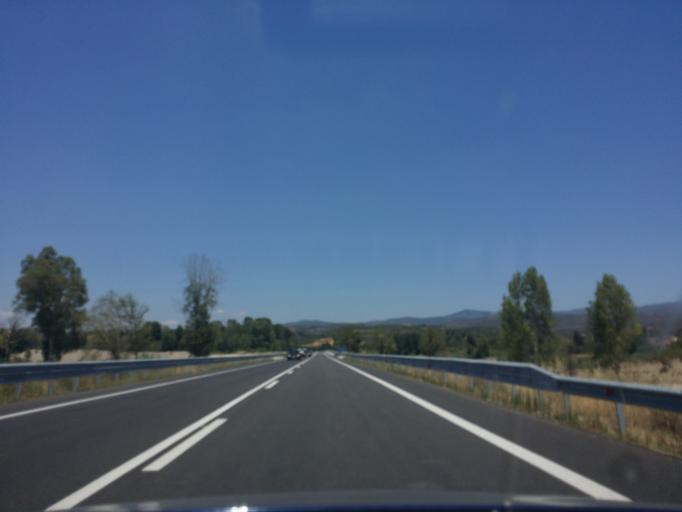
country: GR
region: Peloponnese
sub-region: Nomos Lakonias
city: Sparti
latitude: 37.0091
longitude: 22.4844
